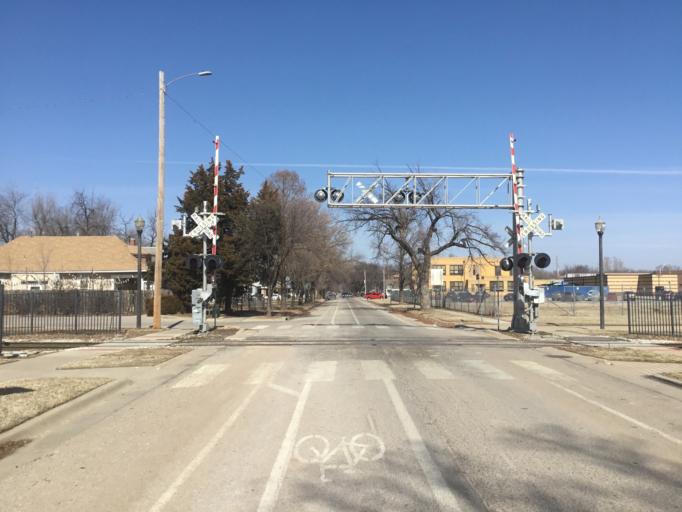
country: US
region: Kansas
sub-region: Sedgwick County
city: Wichita
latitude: 37.6697
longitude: -97.3342
